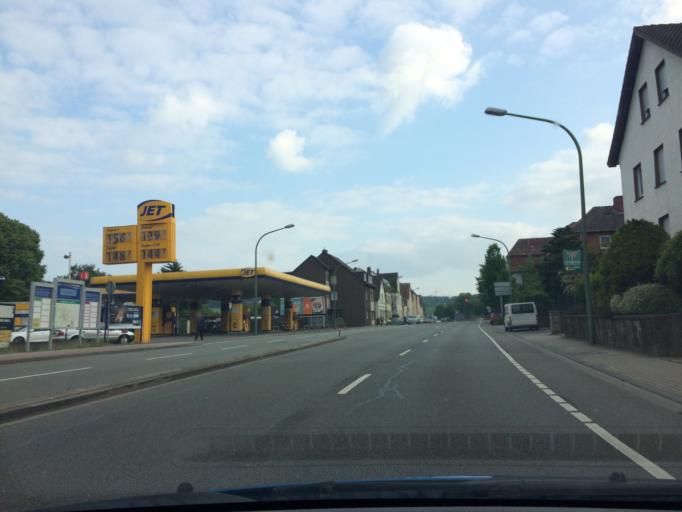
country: DE
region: Lower Saxony
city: Osnabrueck
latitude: 52.2515
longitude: 8.0622
